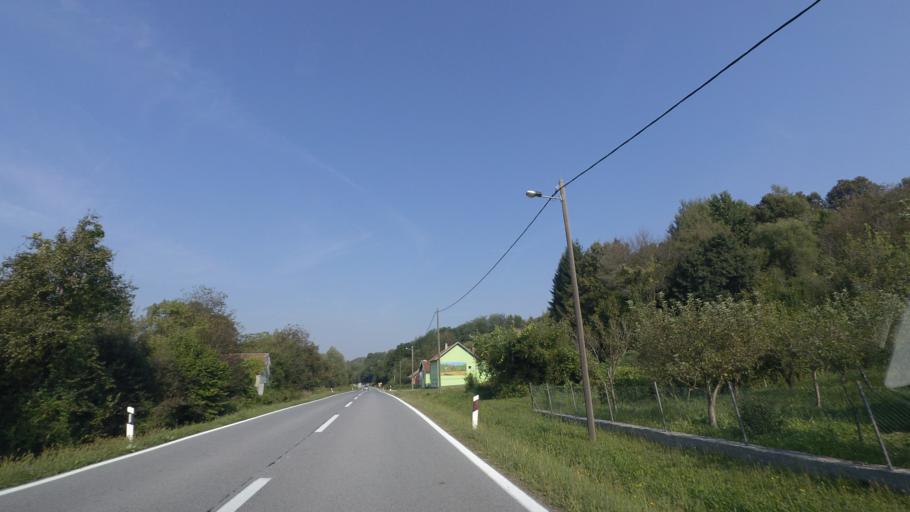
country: HR
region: Bjelovarsko-Bilogorska
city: Sirac
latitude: 45.4698
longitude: 17.3352
